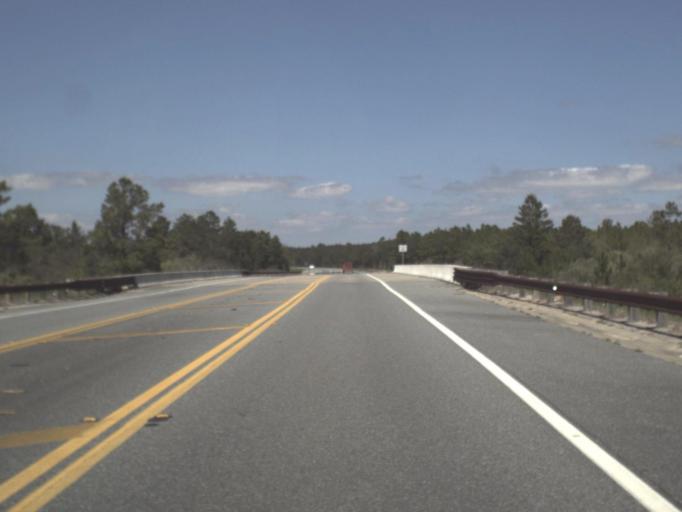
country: US
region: Florida
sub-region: Gulf County
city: Port Saint Joe
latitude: 29.8712
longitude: -85.3391
